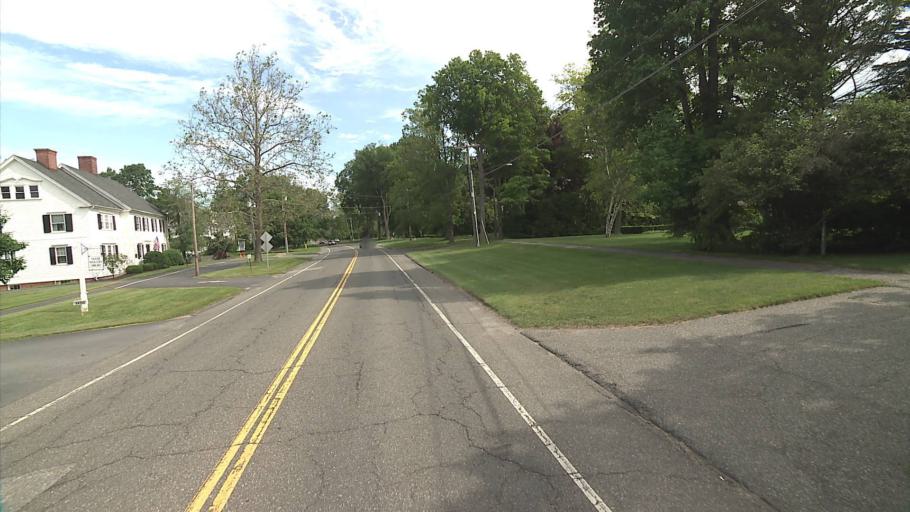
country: US
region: Connecticut
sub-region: Litchfield County
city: Litchfield
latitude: 41.7410
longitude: -73.1872
